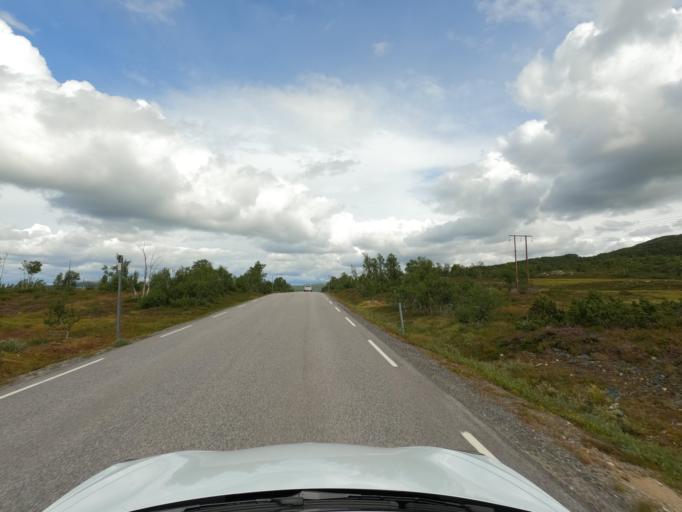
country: NO
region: Telemark
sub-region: Tinn
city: Rjukan
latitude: 59.8014
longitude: 8.2658
